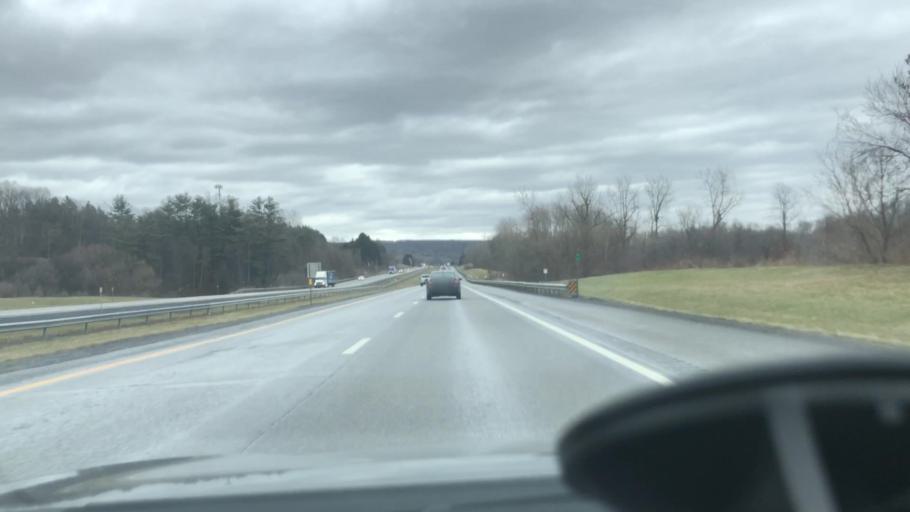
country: US
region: New York
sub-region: Herkimer County
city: Frankfort
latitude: 43.0686
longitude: -75.0904
